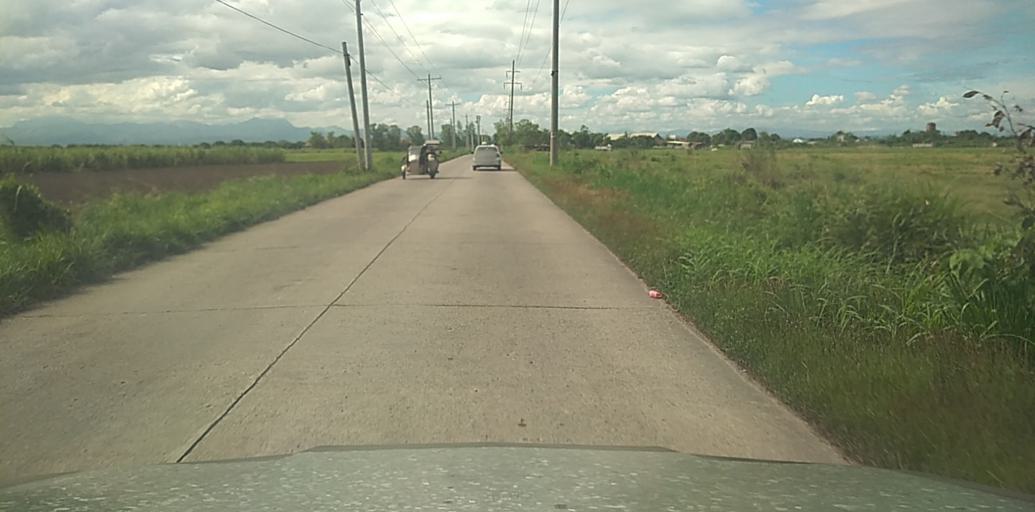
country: PH
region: Central Luzon
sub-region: Province of Pampanga
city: Arenas
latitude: 15.1746
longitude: 120.6726
